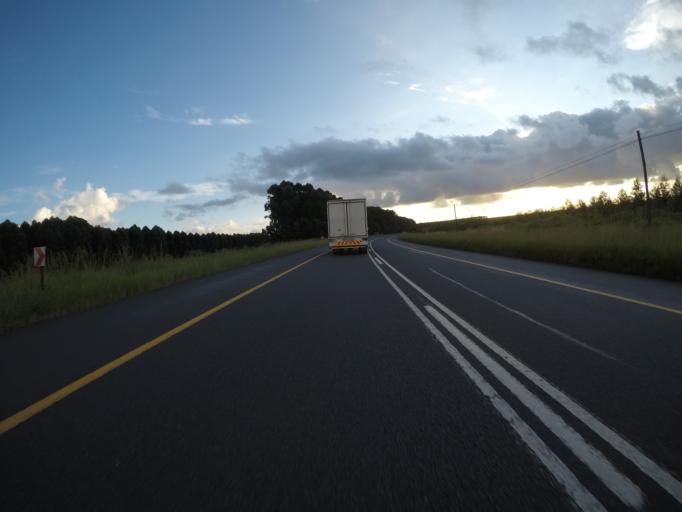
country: ZA
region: KwaZulu-Natal
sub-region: uThungulu District Municipality
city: KwaMbonambi
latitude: -28.5763
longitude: 32.1056
